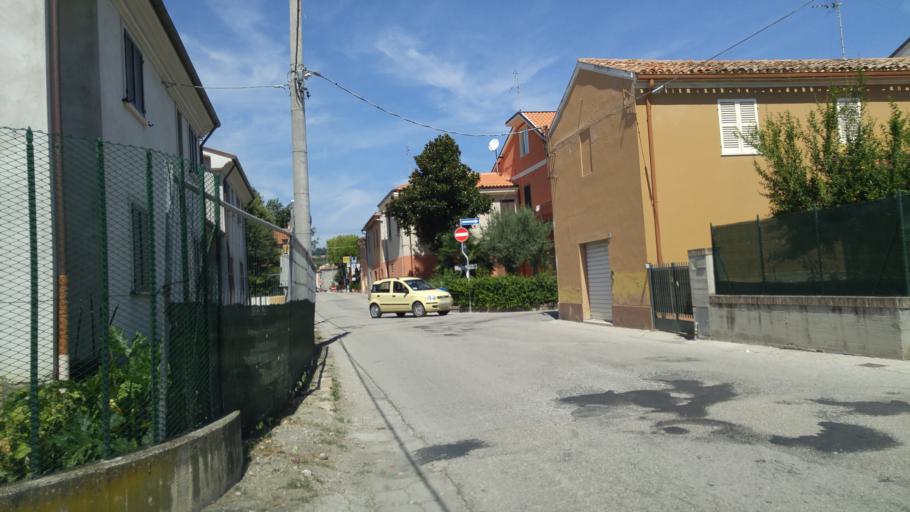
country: IT
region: The Marches
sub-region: Provincia di Pesaro e Urbino
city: Bellocchi
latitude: 43.7984
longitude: 12.9959
